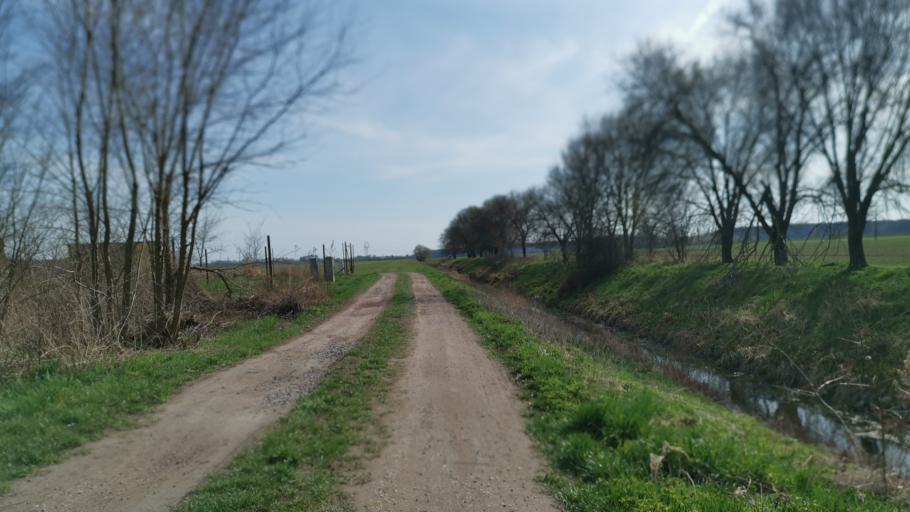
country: CZ
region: South Moravian
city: Tvrdonice
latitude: 48.7257
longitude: 17.0216
